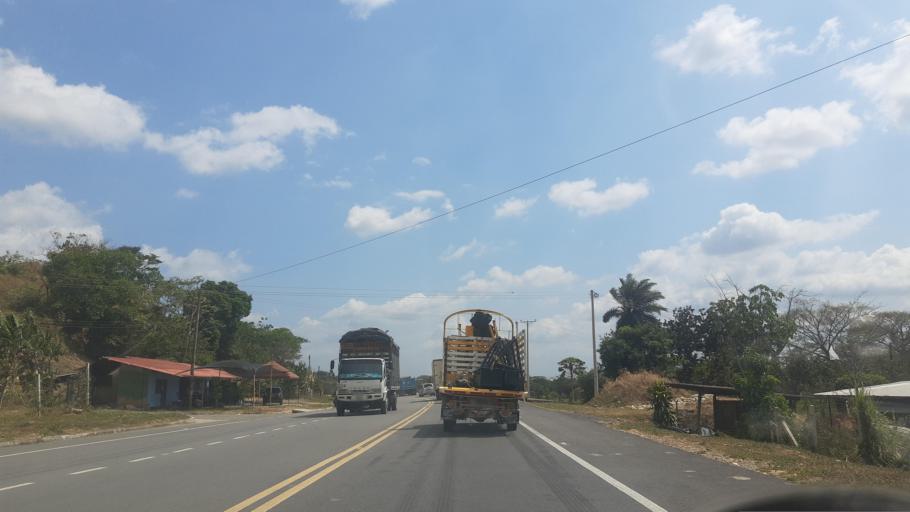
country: CO
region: Casanare
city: Tauramena
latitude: 5.0211
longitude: -72.6621
